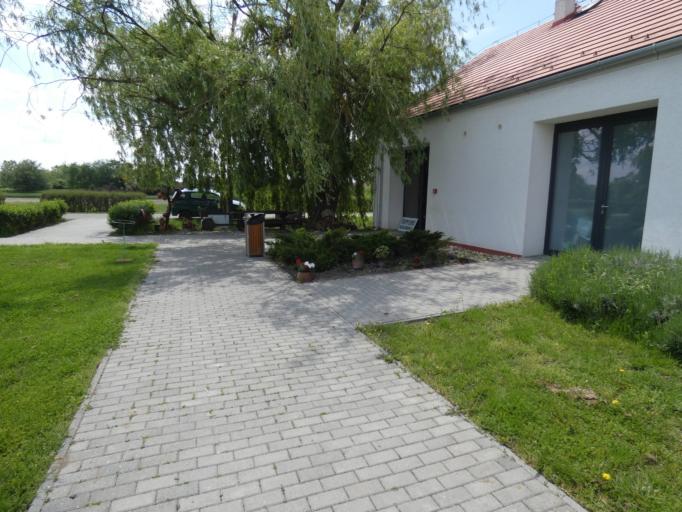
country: HU
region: Hajdu-Bihar
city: Hortobagy
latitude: 47.5946
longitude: 21.1541
